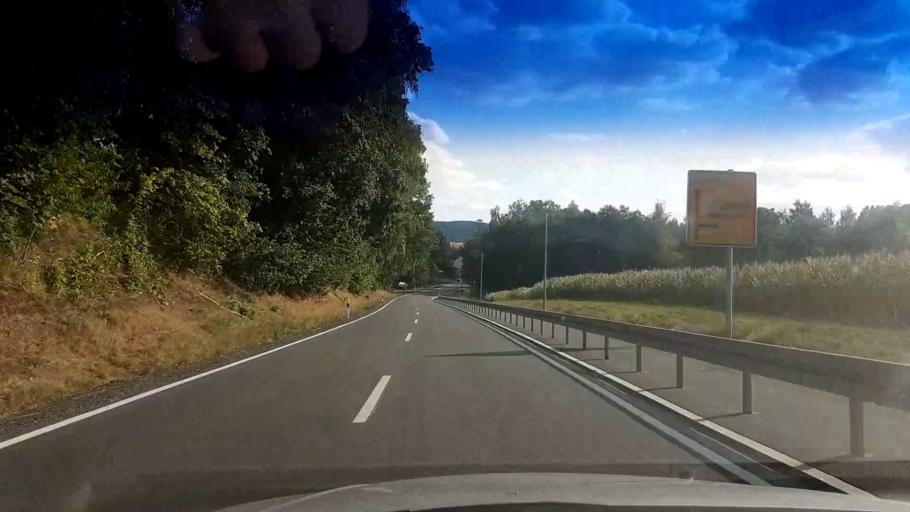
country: DE
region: Bavaria
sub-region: Upper Palatinate
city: Neualbenreuth
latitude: 49.9722
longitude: 12.4449
